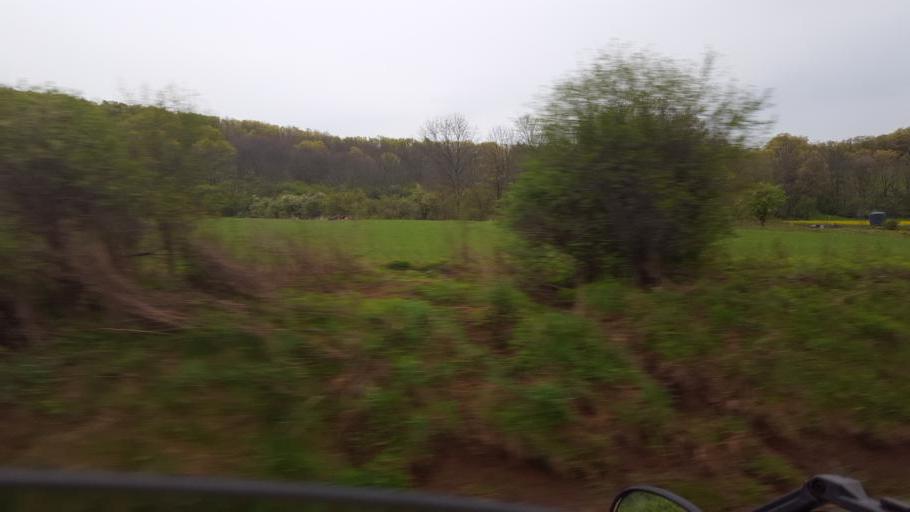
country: US
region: New York
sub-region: Allegany County
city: Andover
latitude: 41.9303
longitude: -77.7995
